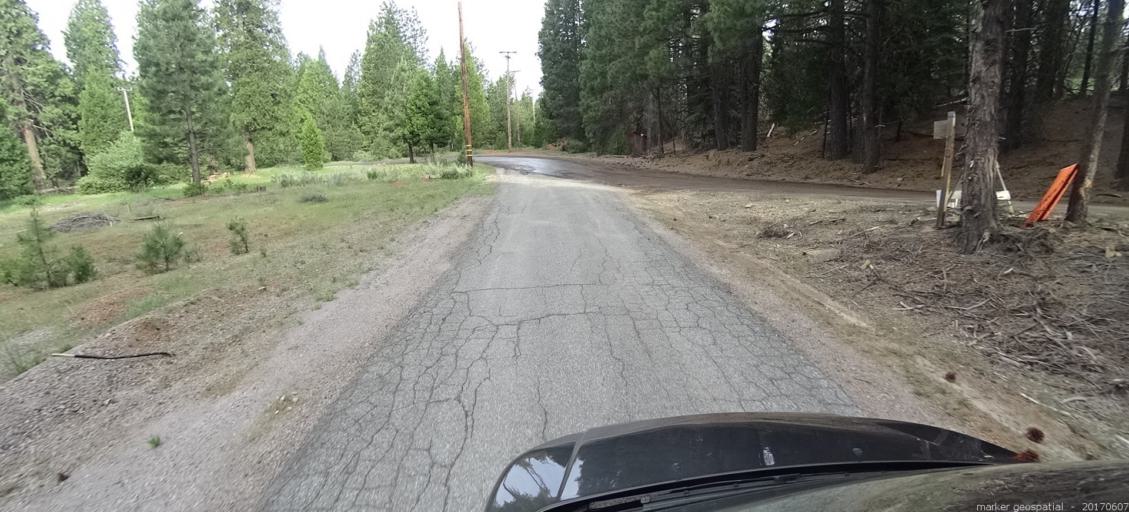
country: US
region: California
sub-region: Shasta County
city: Burney
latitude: 41.1998
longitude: -121.6827
